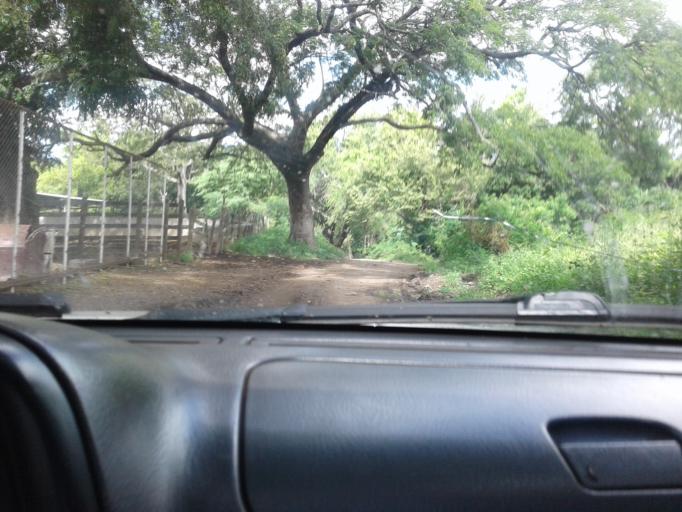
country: NI
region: Matagalpa
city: Ciudad Dario
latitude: 12.8420
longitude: -86.1499
